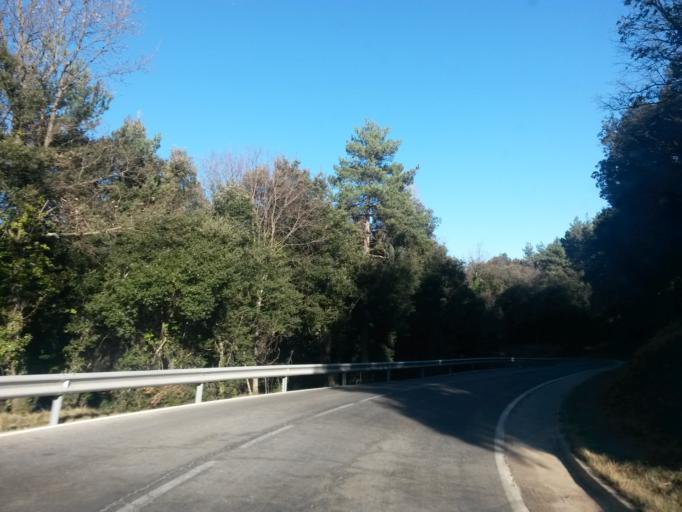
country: ES
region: Catalonia
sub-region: Provincia de Girona
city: Bas
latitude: 42.0893
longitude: 2.4702
